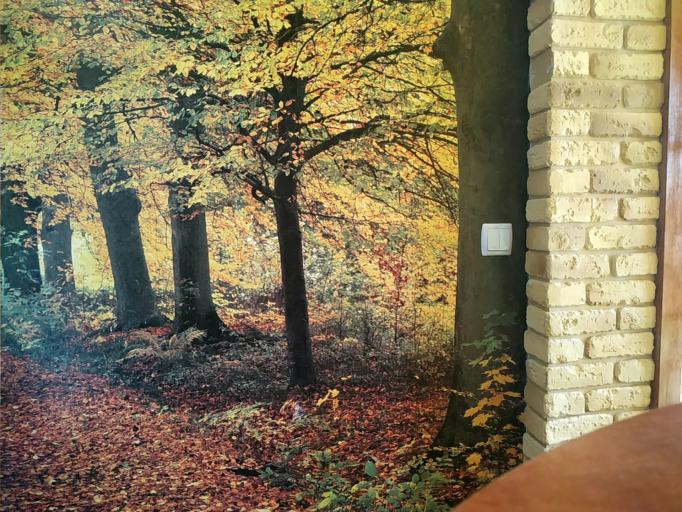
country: RU
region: Vologda
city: Molochnoye
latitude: 58.9435
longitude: 39.6557
